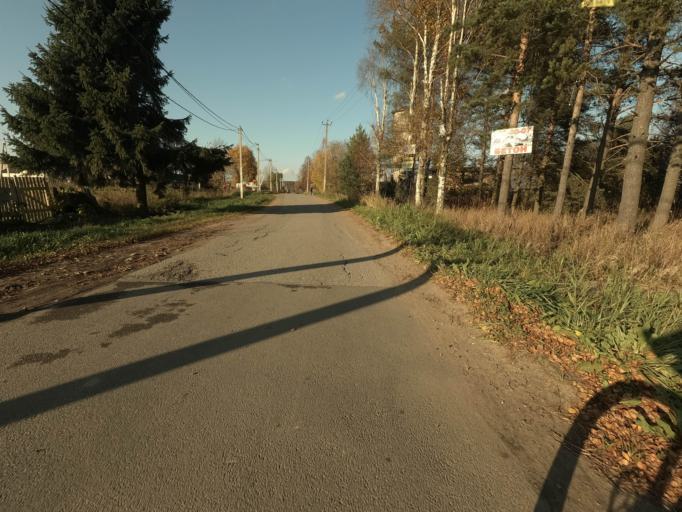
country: RU
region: Leningrad
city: Luppolovo
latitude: 60.1349
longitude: 30.2571
